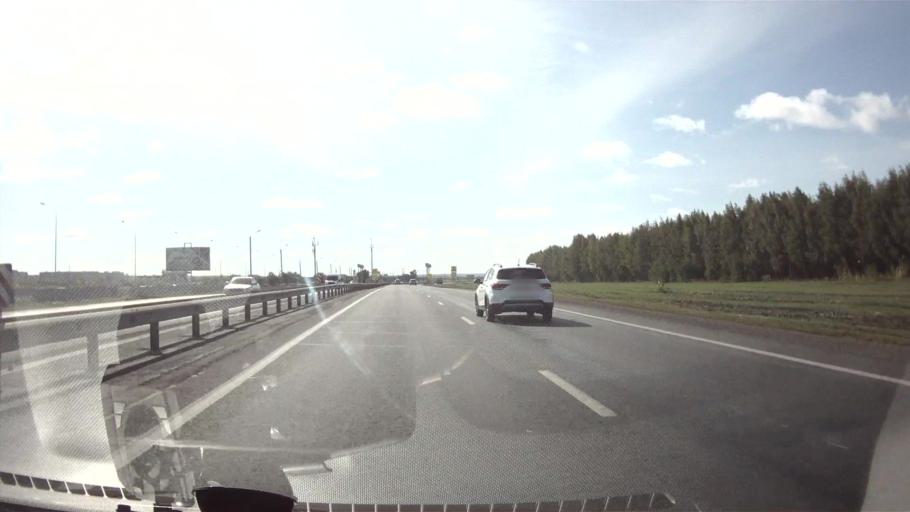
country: RU
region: Ulyanovsk
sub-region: Ulyanovskiy Rayon
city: Ulyanovsk
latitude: 54.2788
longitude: 48.2591
